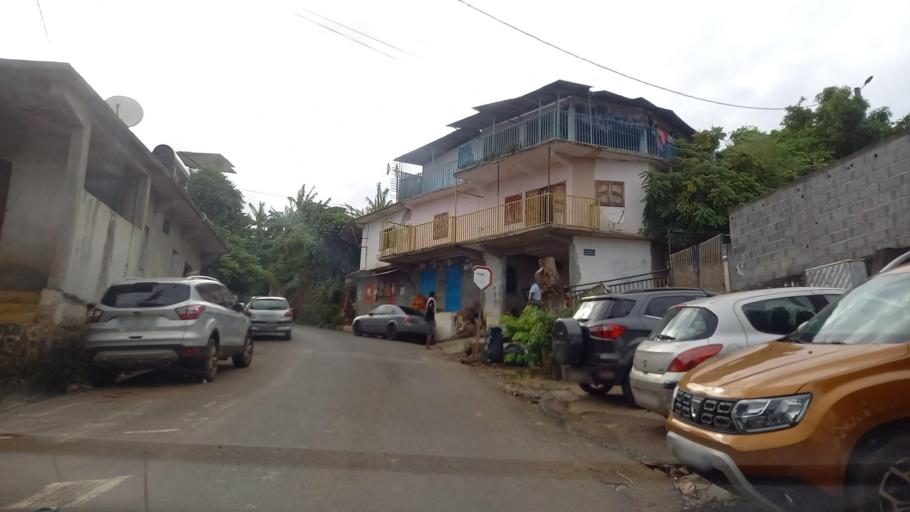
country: YT
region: Sada
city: Sada
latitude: -12.8532
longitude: 45.0973
